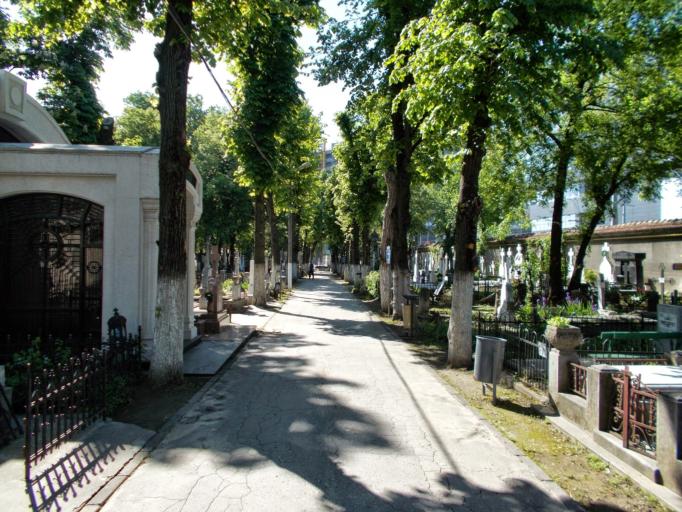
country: RO
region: Bucuresti
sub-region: Municipiul Bucuresti
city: Bucuresti
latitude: 44.4028
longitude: 26.0985
